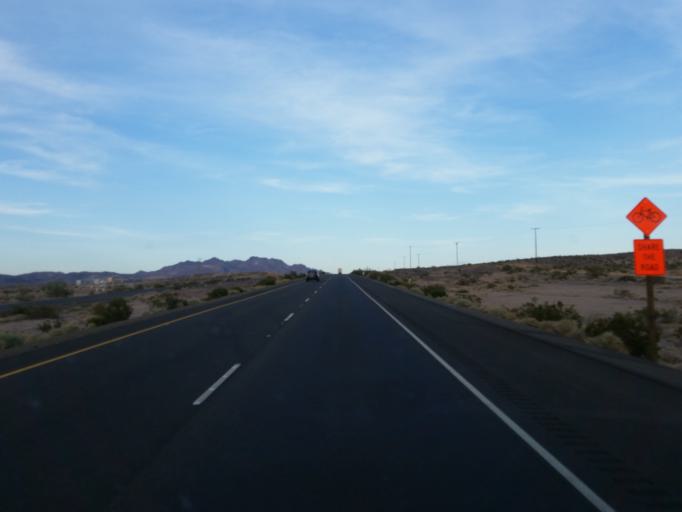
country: US
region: California
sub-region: San Bernardino County
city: Fort Irwin
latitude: 34.7850
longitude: -116.4283
